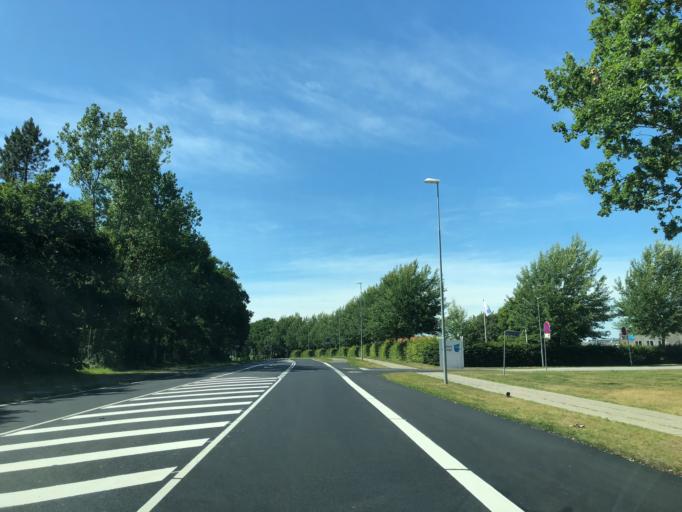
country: DK
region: Central Jutland
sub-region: Skive Kommune
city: Skive
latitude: 56.5541
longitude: 9.0193
